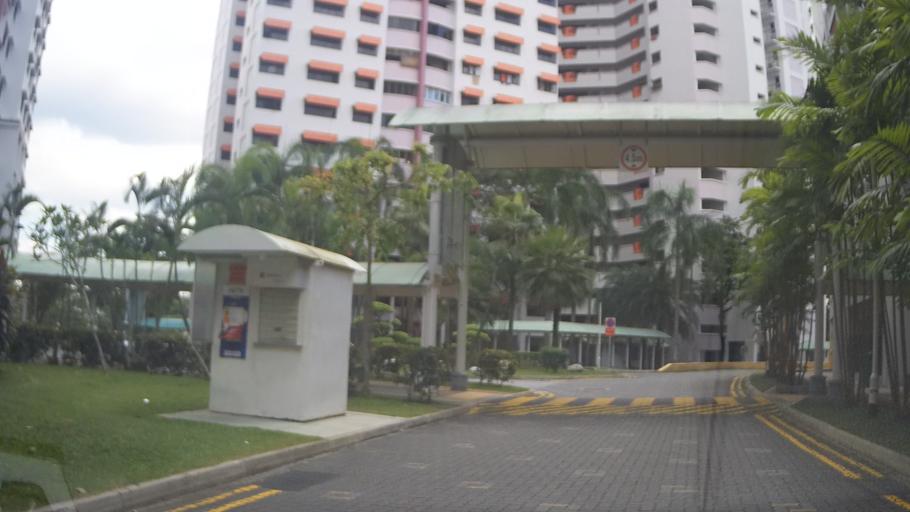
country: MY
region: Johor
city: Johor Bahru
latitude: 1.4027
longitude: 103.7514
